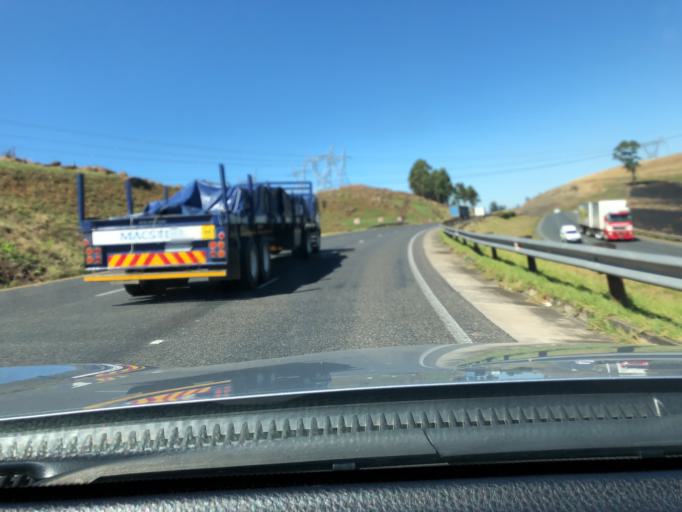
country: ZA
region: KwaZulu-Natal
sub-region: uMgungundlovu District Municipality
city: Howick
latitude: -29.4403
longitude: 30.1751
